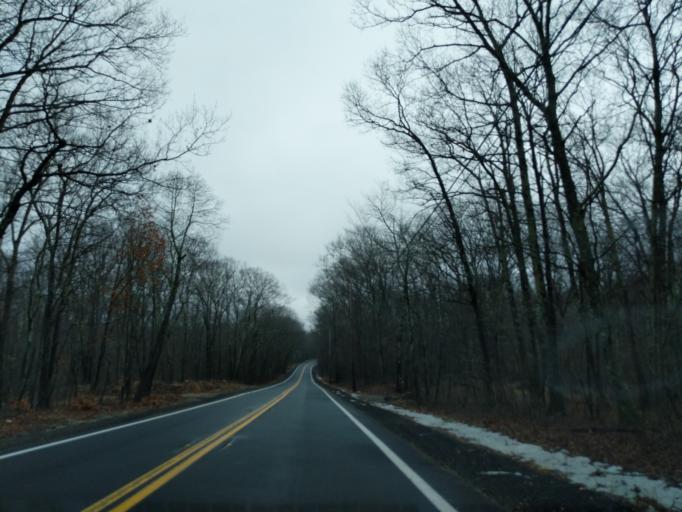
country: US
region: Massachusetts
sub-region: Worcester County
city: Douglas
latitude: 42.0572
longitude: -71.8054
